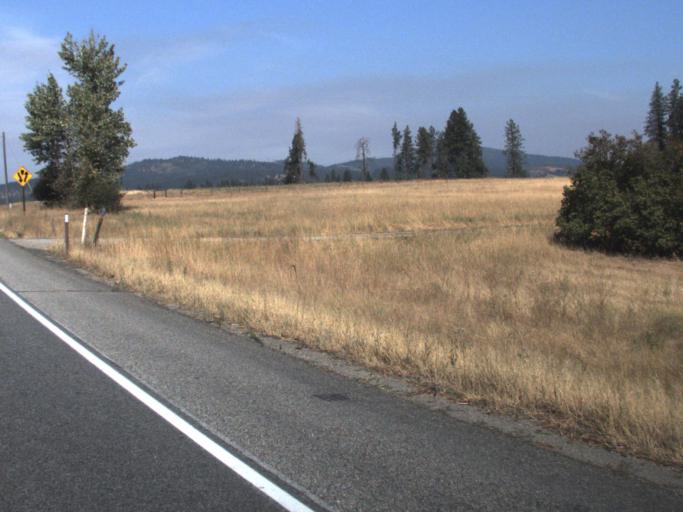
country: US
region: Washington
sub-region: Spokane County
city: Deer Park
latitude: 48.0383
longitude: -117.3492
